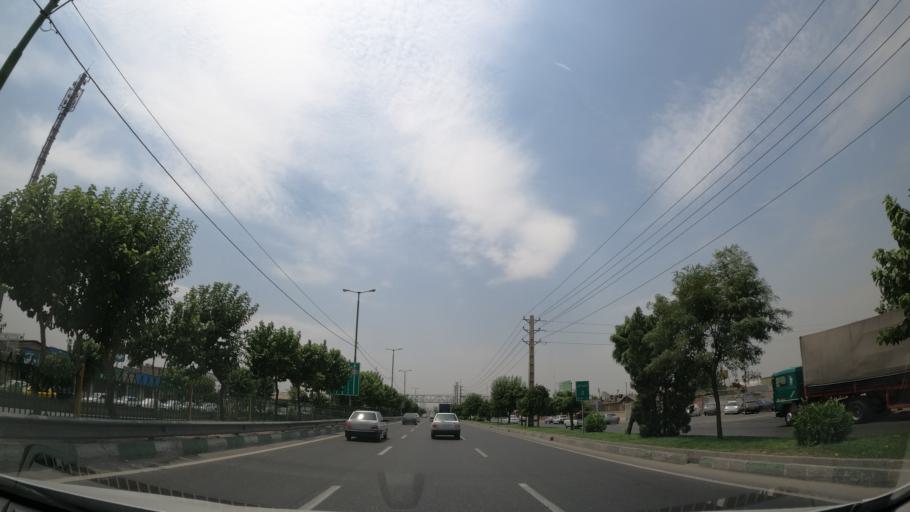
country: IR
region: Tehran
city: Eslamshahr
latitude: 35.6764
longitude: 51.2875
